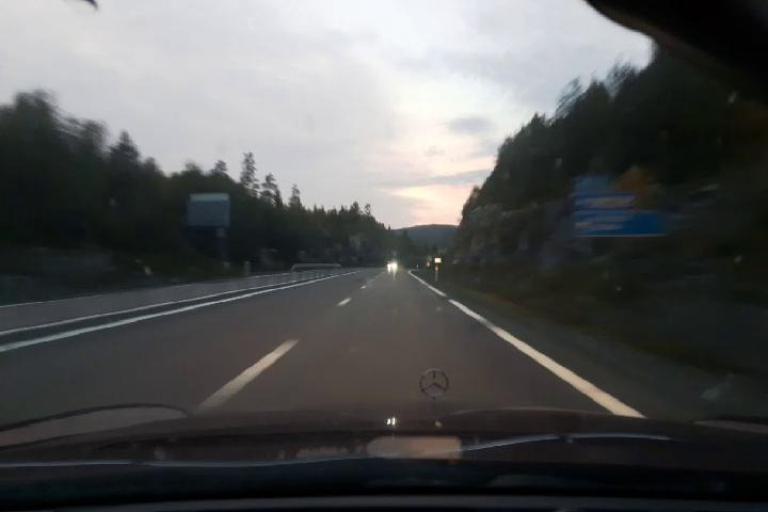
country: SE
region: Vaesternorrland
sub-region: Kramfors Kommun
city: Nordingra
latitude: 62.9482
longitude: 18.0936
